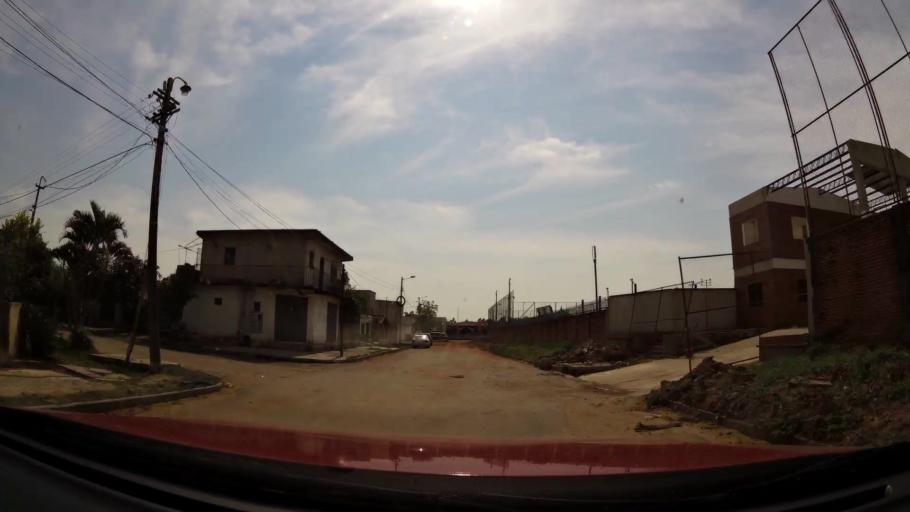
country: PY
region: Central
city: Fernando de la Mora
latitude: -25.2745
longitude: -57.5466
